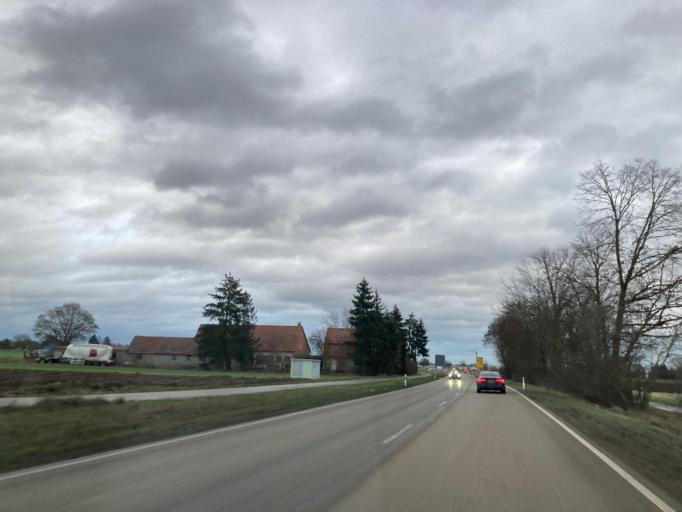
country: DE
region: Baden-Wuerttemberg
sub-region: Tuebingen Region
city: Langenau
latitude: 48.4926
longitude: 10.0955
